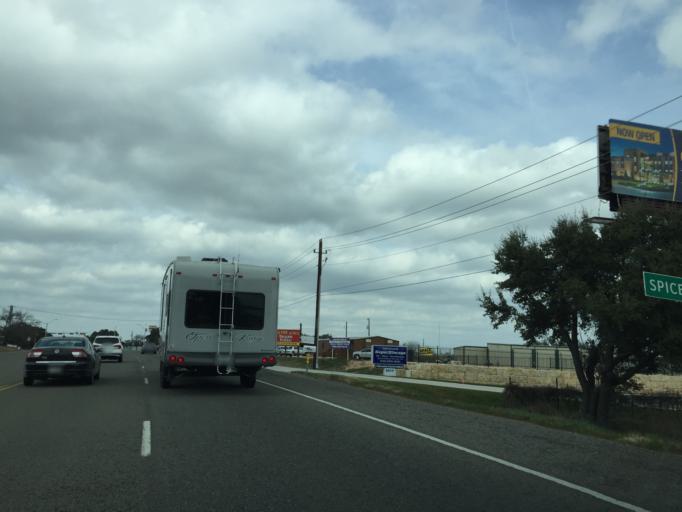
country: US
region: Texas
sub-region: Travis County
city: Briarcliff
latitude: 30.4601
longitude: -98.1572
